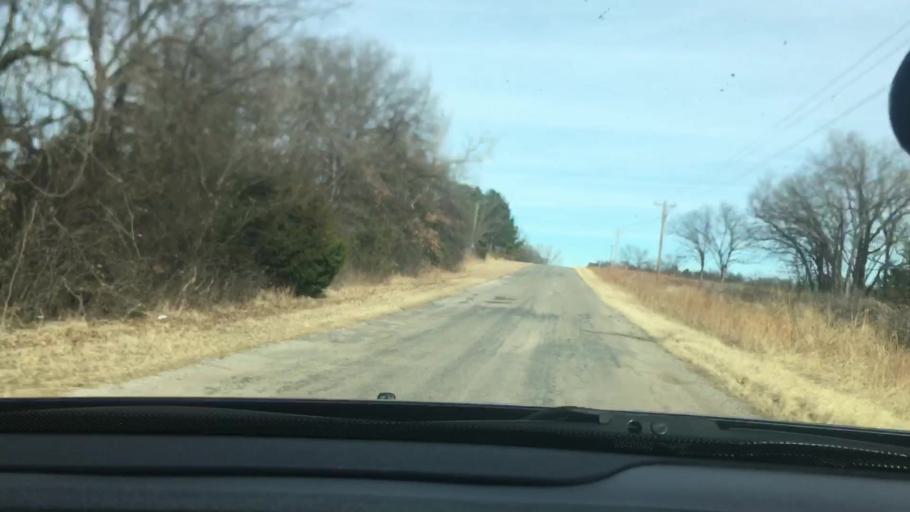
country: US
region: Oklahoma
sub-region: Garvin County
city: Wynnewood
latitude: 34.6420
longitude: -97.2475
